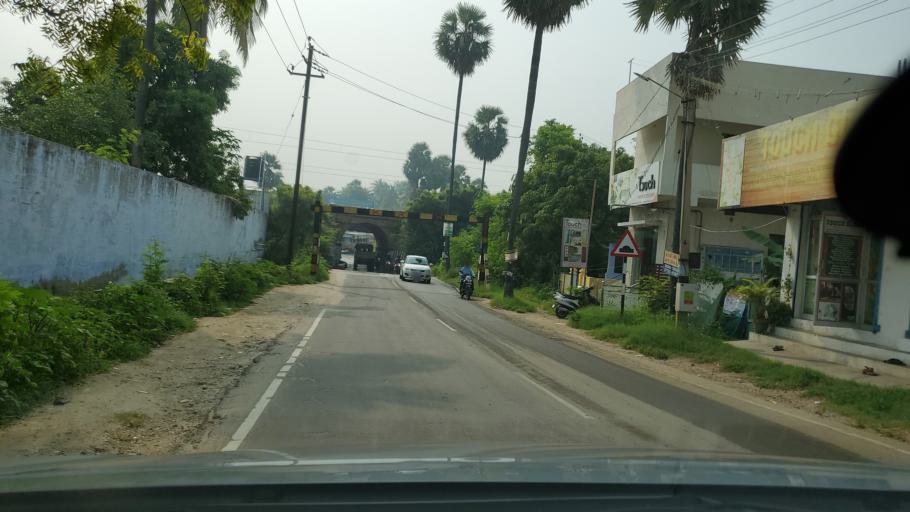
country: IN
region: Tamil Nadu
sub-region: Erode
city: Erode
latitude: 11.3113
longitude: 77.7072
